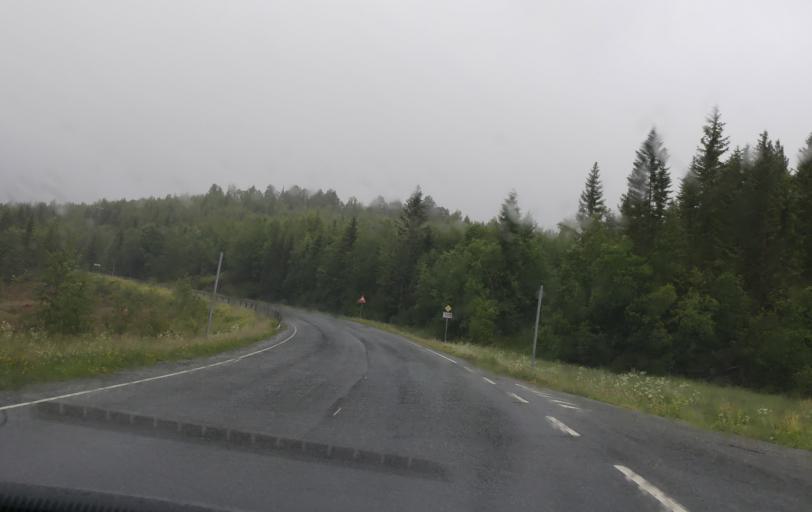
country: NO
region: Sor-Trondelag
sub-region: Selbu
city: Mebonden
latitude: 63.3710
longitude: 11.0714
